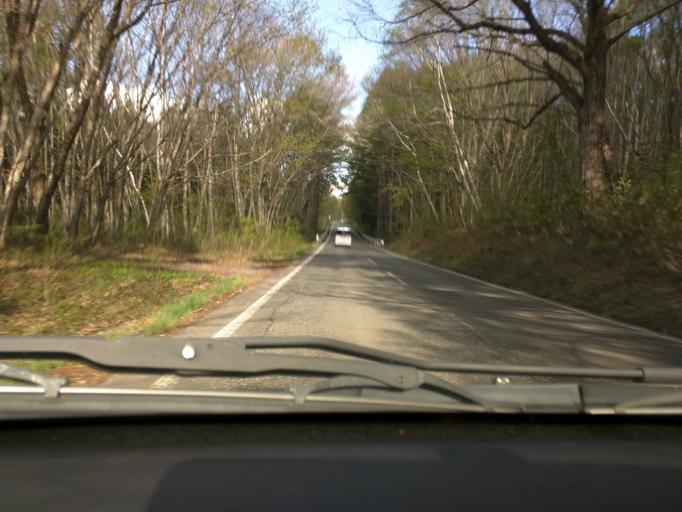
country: JP
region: Nagano
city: Nagano-shi
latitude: 36.7183
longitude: 138.1027
